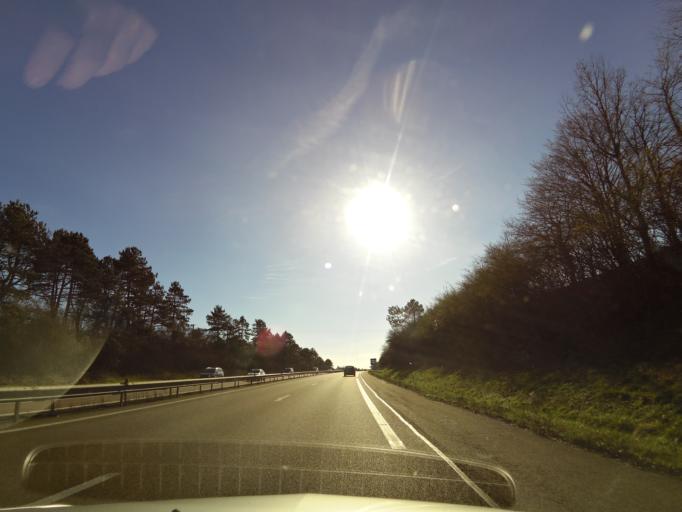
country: FR
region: Bourgogne
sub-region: Departement de l'Yonne
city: Saint-Bris-le-Vineux
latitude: 47.7587
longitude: 3.7297
